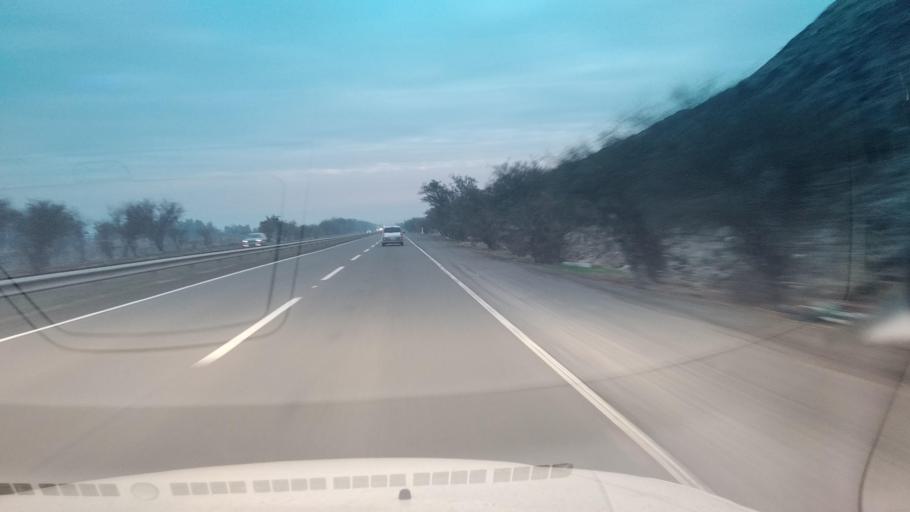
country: CL
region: Santiago Metropolitan
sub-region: Provincia de Chacabuco
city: Chicureo Abajo
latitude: -33.1963
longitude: -70.6583
